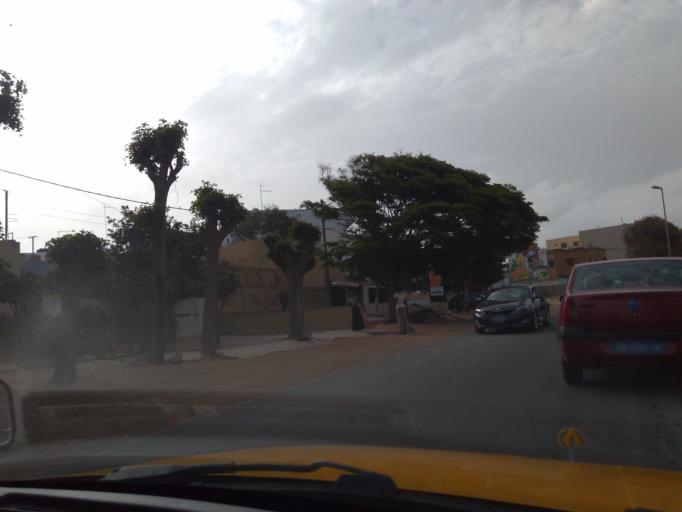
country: SN
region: Dakar
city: Grand Dakar
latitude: 14.7522
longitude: -17.4602
